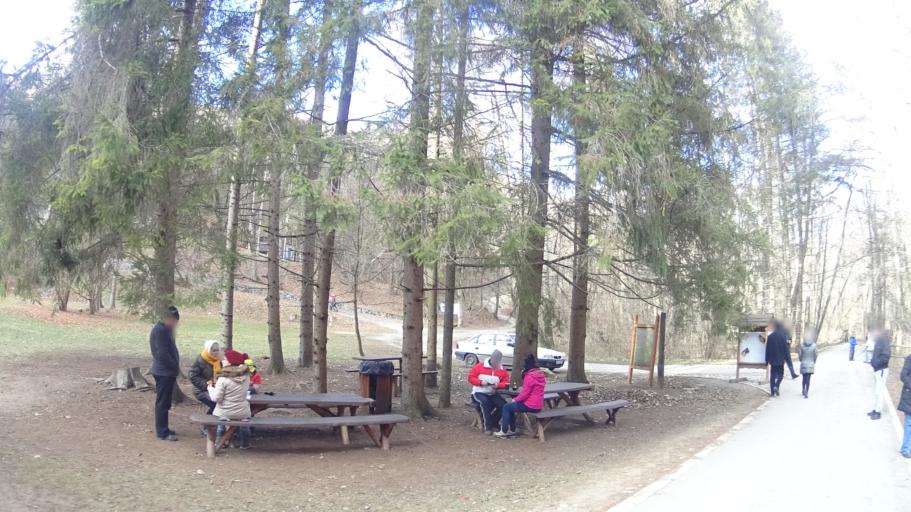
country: HU
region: Heves
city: Szilvasvarad
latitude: 48.0809
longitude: 20.4059
